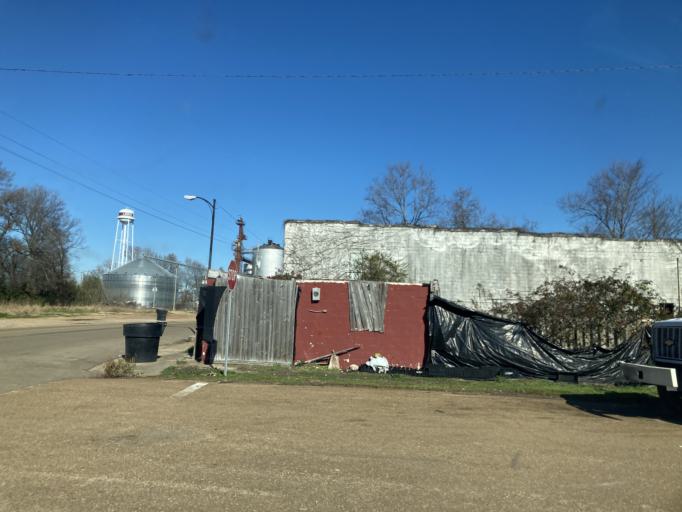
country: US
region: Mississippi
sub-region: Yazoo County
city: Yazoo City
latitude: 32.9808
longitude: -90.5917
